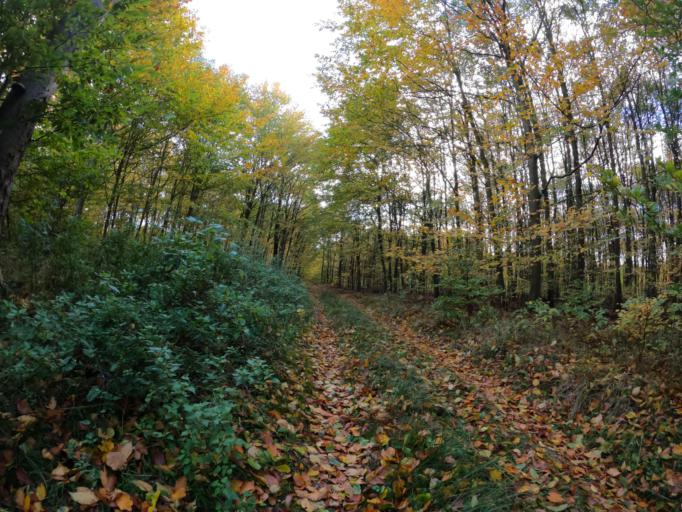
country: PL
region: West Pomeranian Voivodeship
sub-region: Powiat mysliborski
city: Barlinek
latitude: 52.9709
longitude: 15.2287
